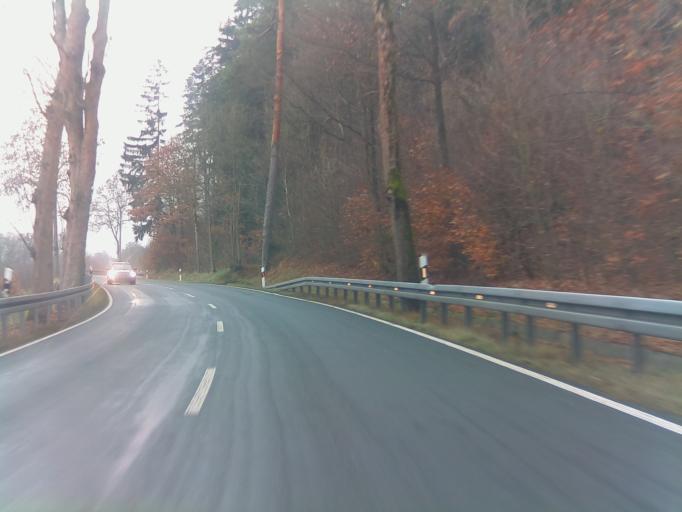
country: DE
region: Thuringia
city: Sankt Kilian
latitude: 50.5272
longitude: 10.8053
